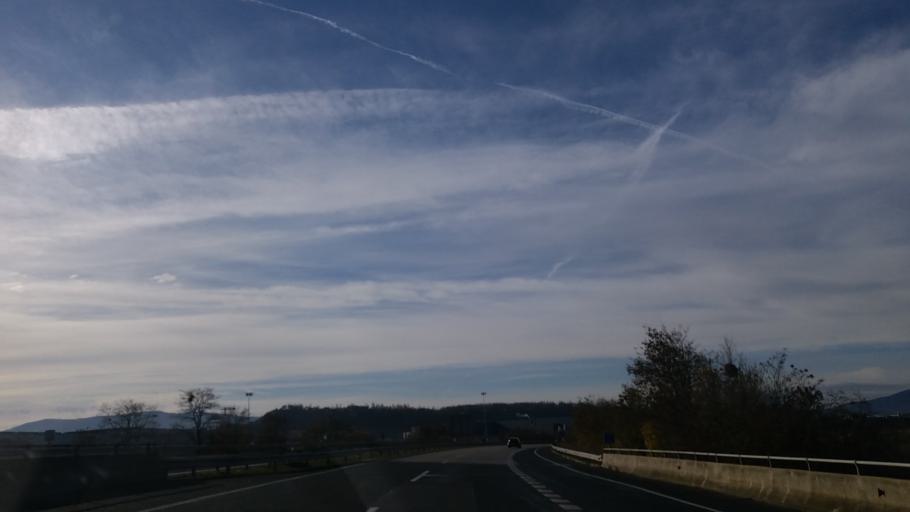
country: ES
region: Navarre
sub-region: Provincia de Navarra
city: Berriobeiti
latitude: 42.8371
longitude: -1.6904
